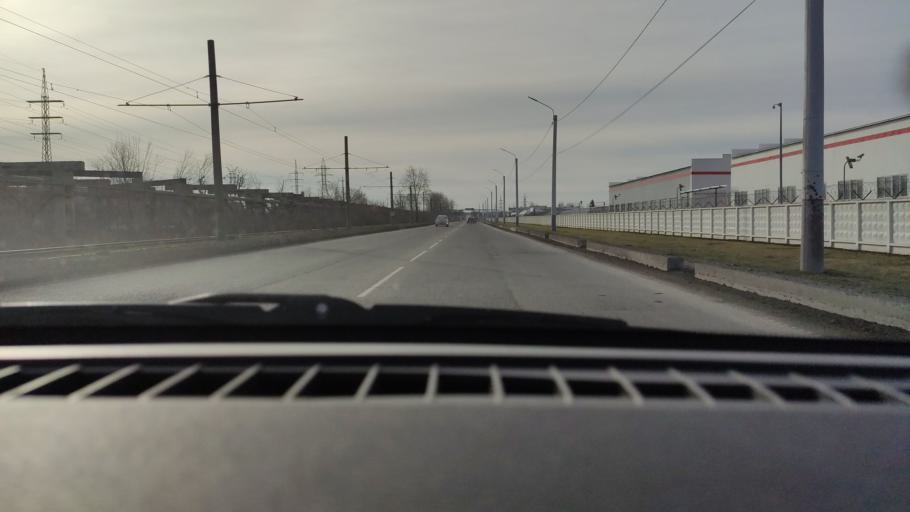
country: RU
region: Perm
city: Gamovo
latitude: 57.9186
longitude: 56.1477
